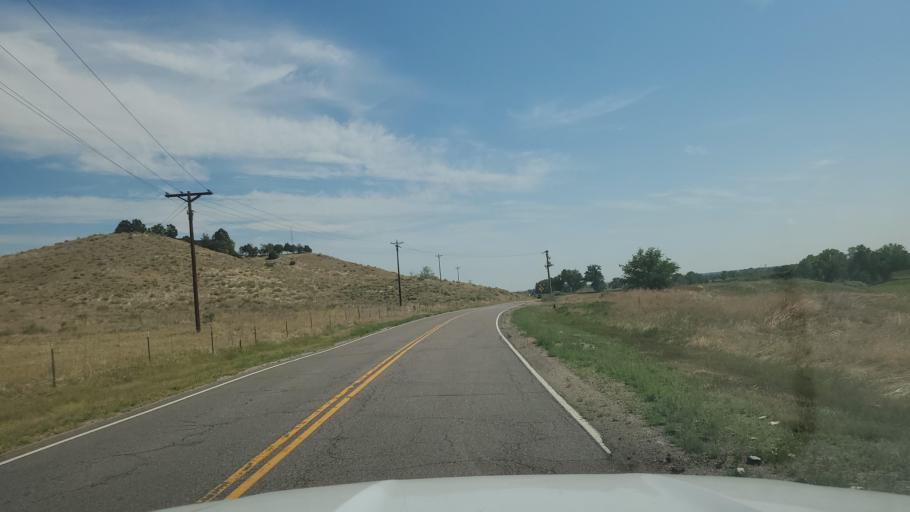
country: US
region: Colorado
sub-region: Adams County
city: Todd Creek
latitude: 39.9389
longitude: -104.8758
